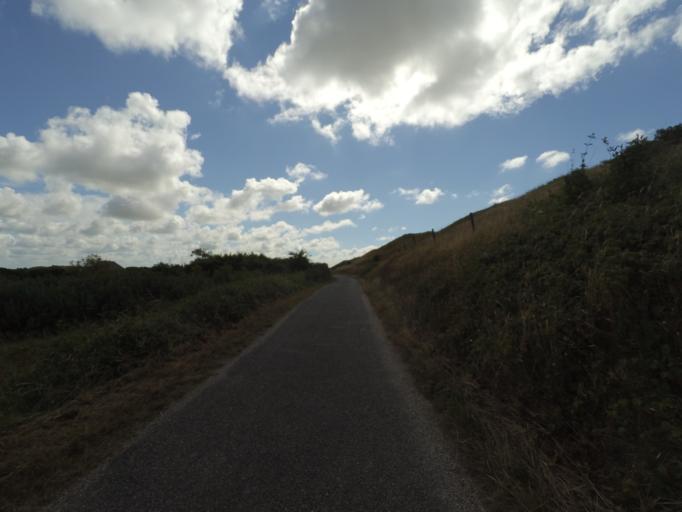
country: NL
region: North Holland
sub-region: Gemeente Texel
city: Den Burg
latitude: 53.1361
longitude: 4.8224
